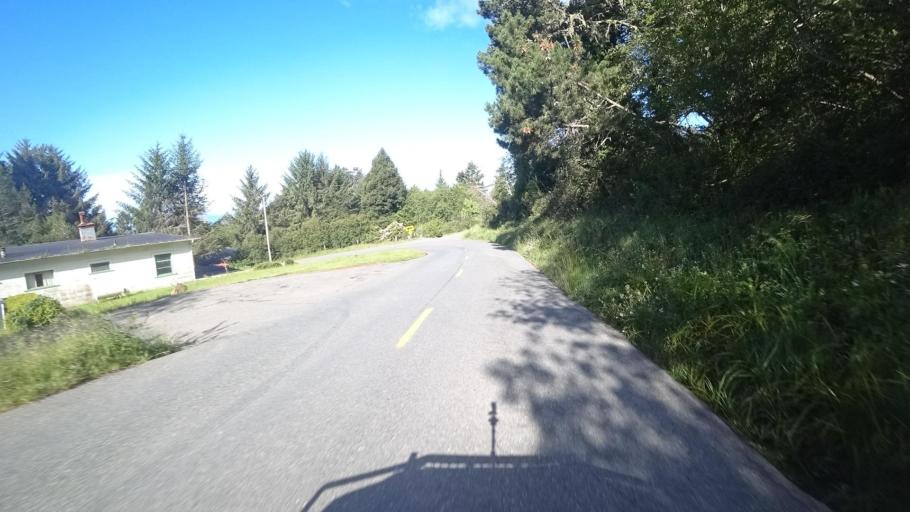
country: US
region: California
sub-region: Humboldt County
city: Westhaven-Moonstone
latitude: 41.0341
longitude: -124.1096
